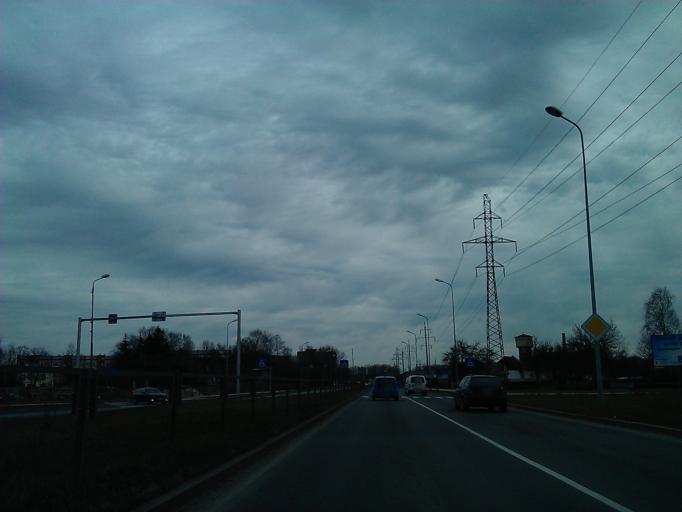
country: LV
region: Riga
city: Riga
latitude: 56.9460
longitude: 24.1646
